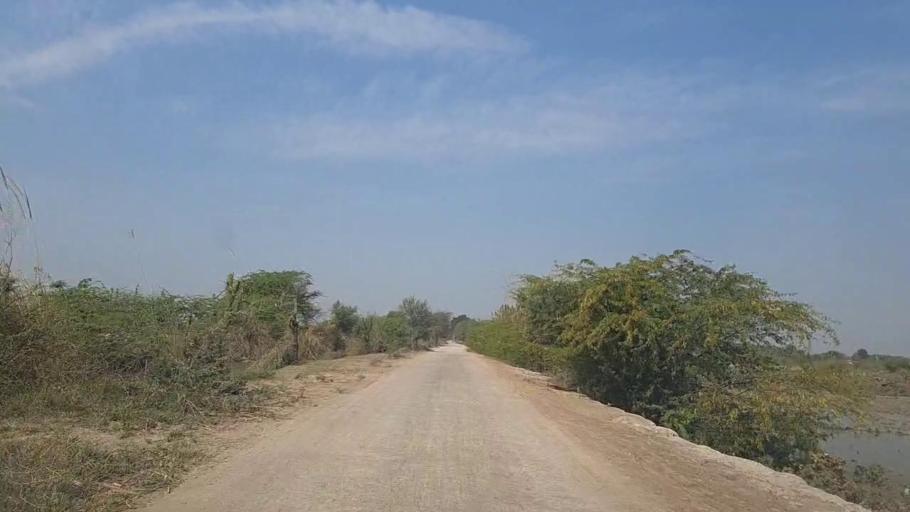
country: PK
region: Sindh
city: Mirpur Khas
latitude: 25.4817
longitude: 68.9307
